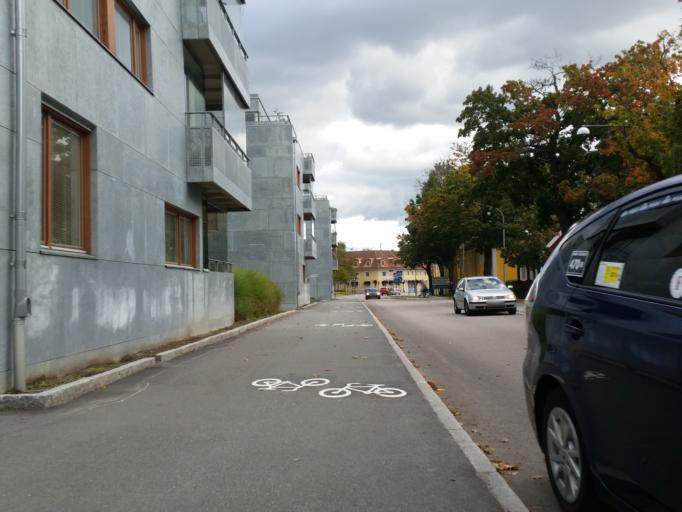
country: SE
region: Stockholm
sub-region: Stockholms Kommun
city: Arsta
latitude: 59.2811
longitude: 18.1066
